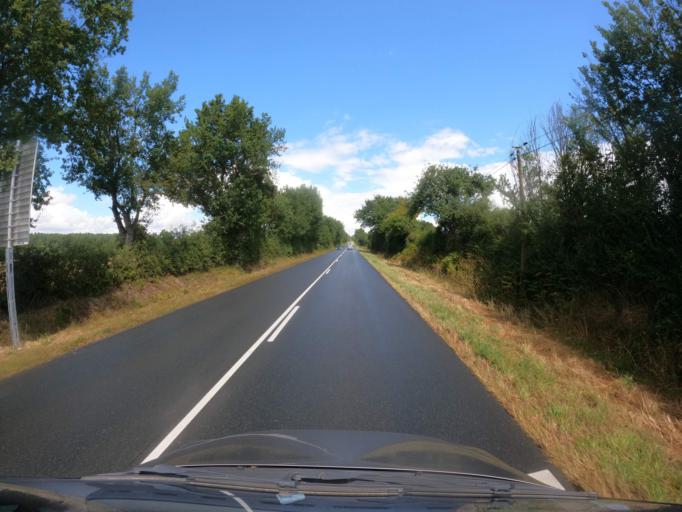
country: FR
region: Pays de la Loire
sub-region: Departement de Maine-et-Loire
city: Feneu
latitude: 47.6021
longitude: -0.5873
